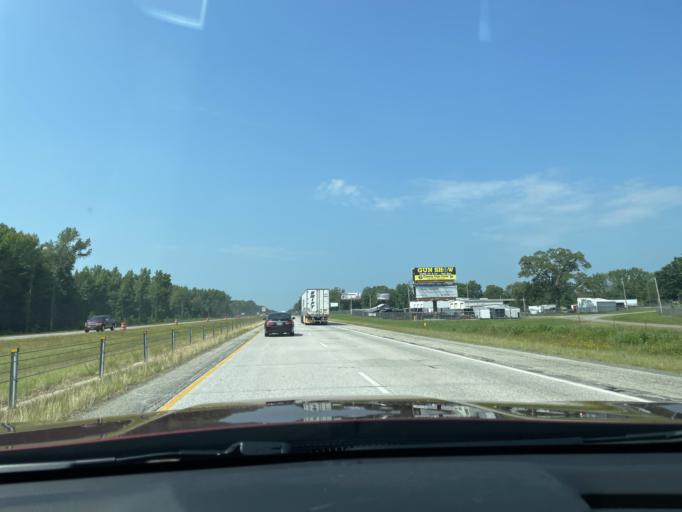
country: US
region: Arkansas
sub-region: White County
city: Searcy
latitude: 35.1956
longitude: -91.7420
